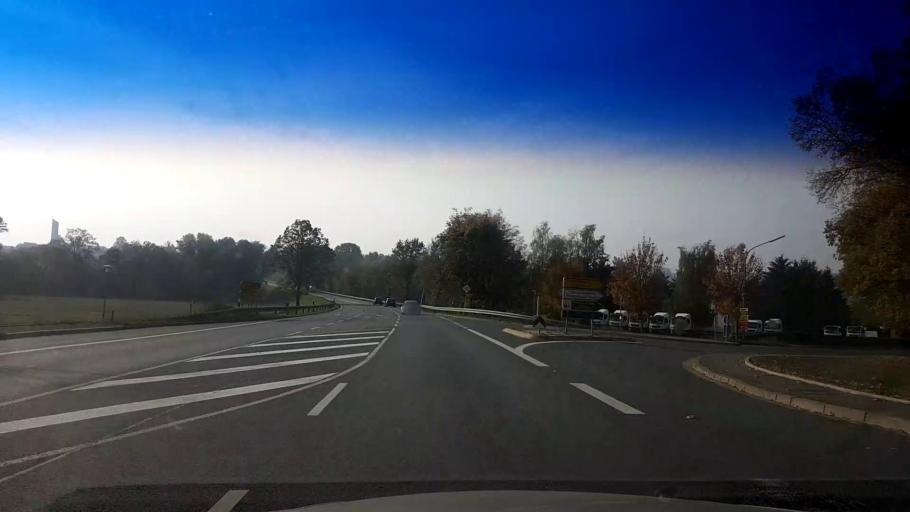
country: DE
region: Bavaria
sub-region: Upper Franconia
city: Himmelkron
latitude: 50.0666
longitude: 11.6043
